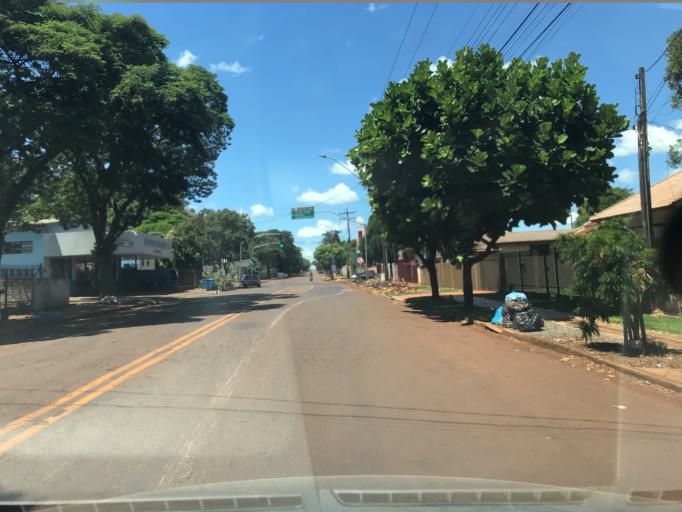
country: BR
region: Parana
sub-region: Palotina
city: Palotina
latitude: -24.2906
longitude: -53.8450
